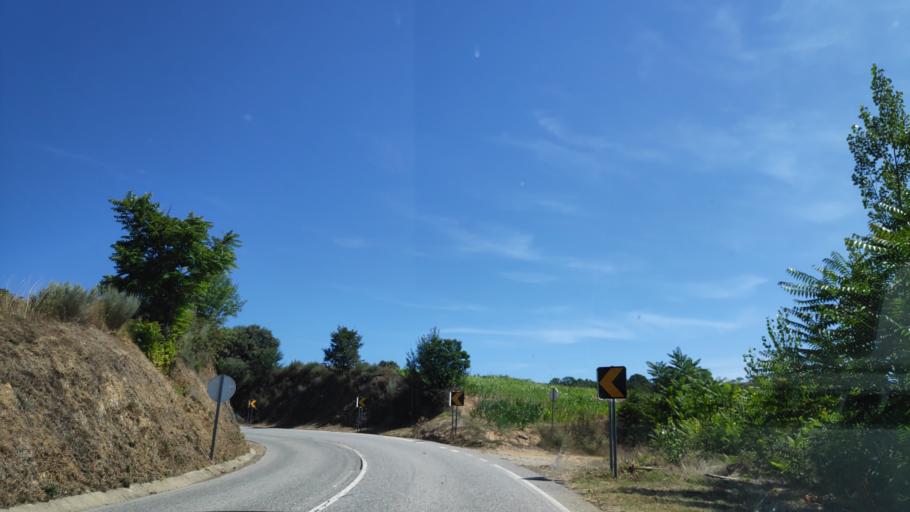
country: PT
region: Braganca
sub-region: Braganca Municipality
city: Braganca
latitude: 41.8587
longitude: -6.7470
